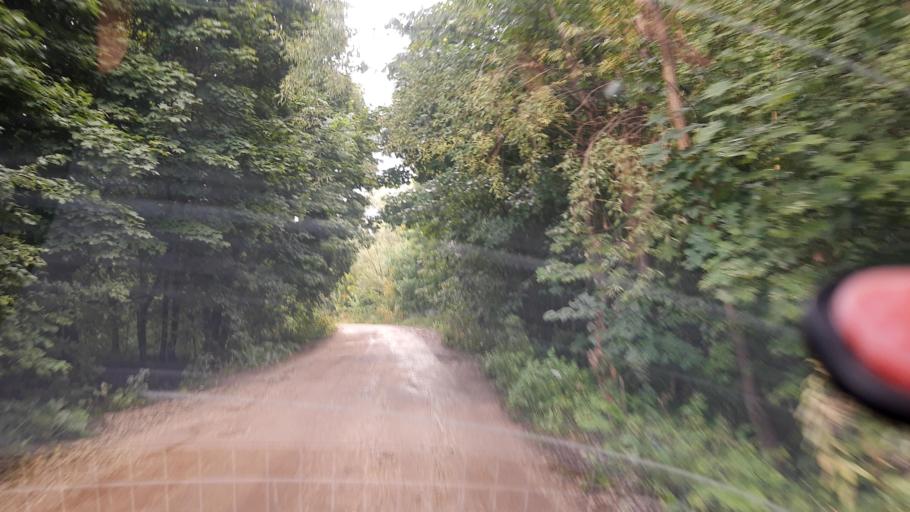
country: RU
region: Bashkortostan
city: Iglino
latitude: 54.7689
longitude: 56.4536
